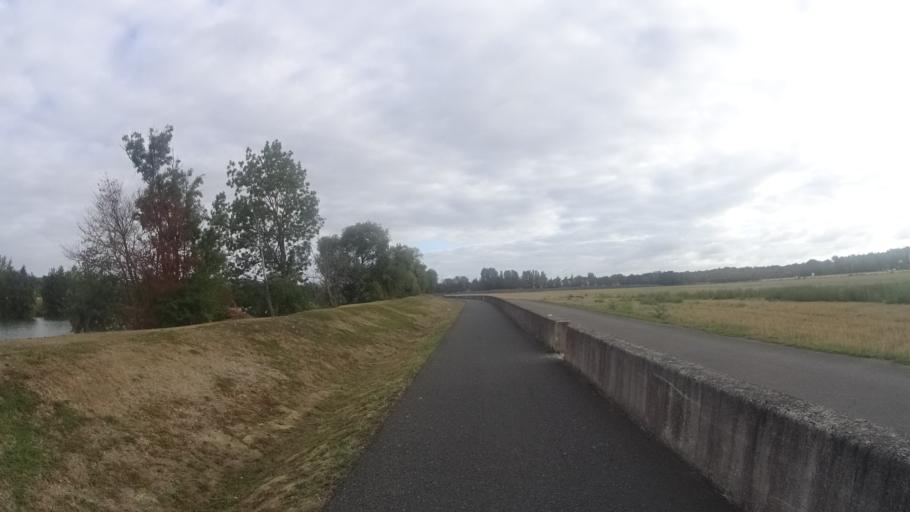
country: FR
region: Picardie
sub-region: Departement de l'Oise
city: Lacroix-Saint-Ouen
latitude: 49.3638
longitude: 2.7678
